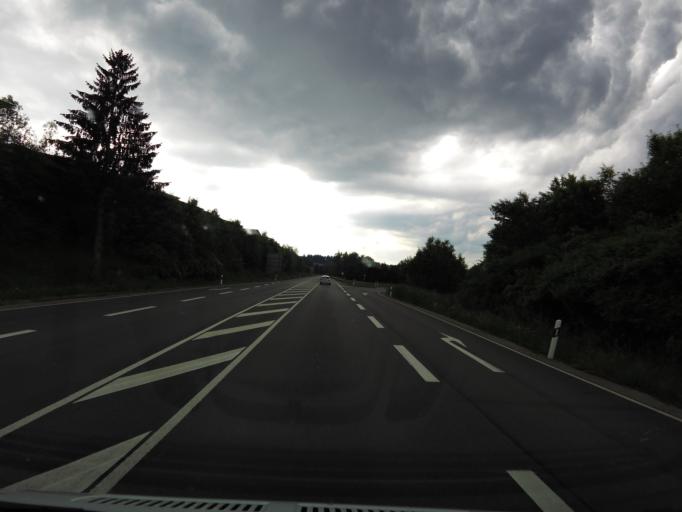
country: DE
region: Bavaria
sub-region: Lower Bavaria
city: Aicha vorm Wald
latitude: 48.6800
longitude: 13.2965
